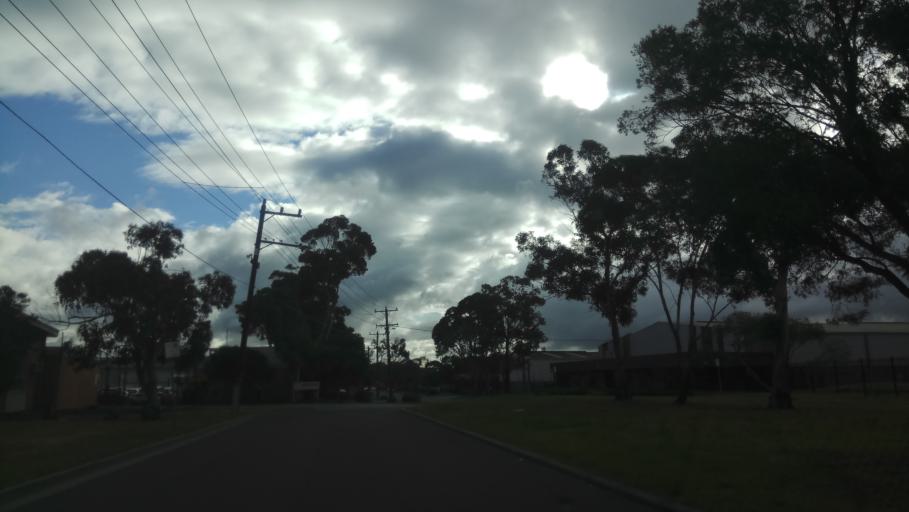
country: AU
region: Victoria
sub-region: Hobsons Bay
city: Altona
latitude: -37.8585
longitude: 144.8089
